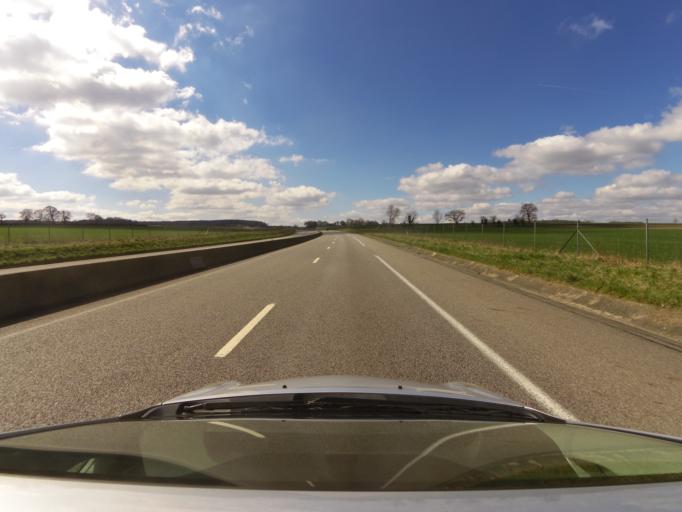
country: FR
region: Haute-Normandie
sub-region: Departement de la Seine-Maritime
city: Neufchatel-en-Bray
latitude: 49.7825
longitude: 1.4793
